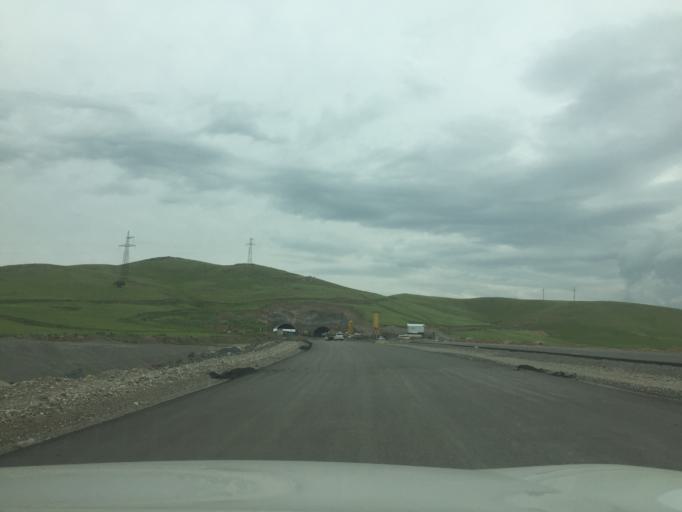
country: KZ
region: Ongtustik Qazaqstan
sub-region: Tulkibas Audany
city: Zhabagly
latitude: 42.5169
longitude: 70.5623
